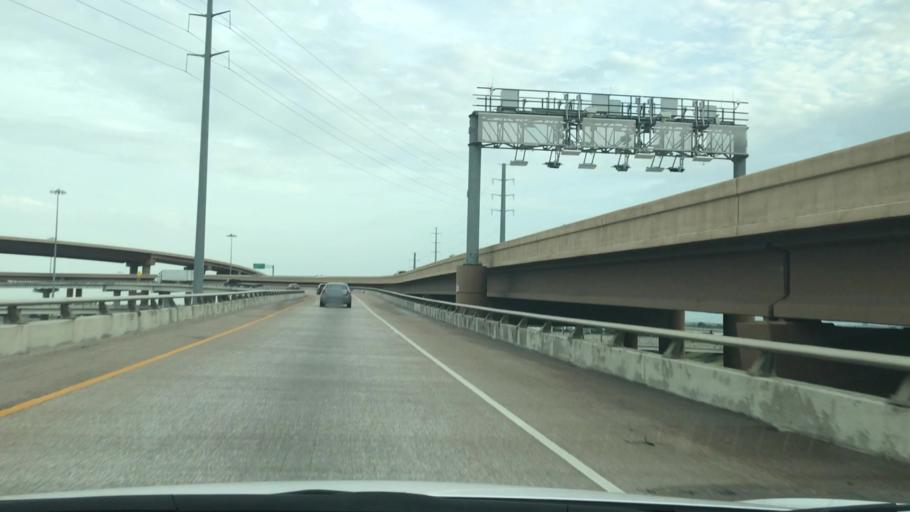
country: US
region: Texas
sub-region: Dallas County
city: Farmers Branch
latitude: 32.9110
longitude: -96.8994
